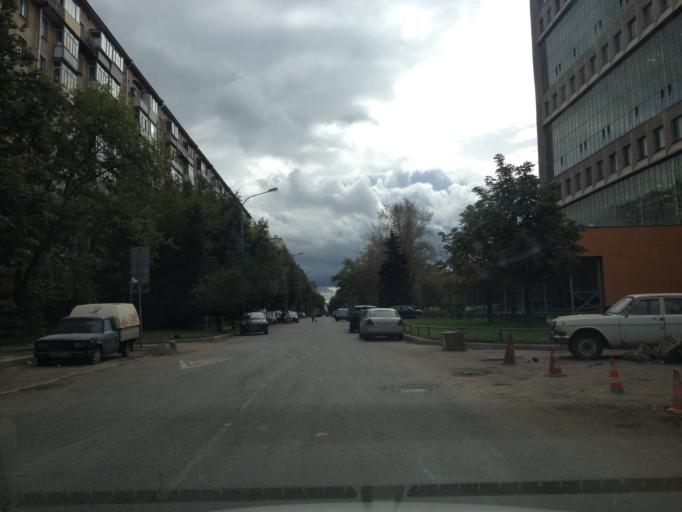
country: RU
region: Moscow
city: Metrogorodok
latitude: 55.8064
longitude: 37.8049
